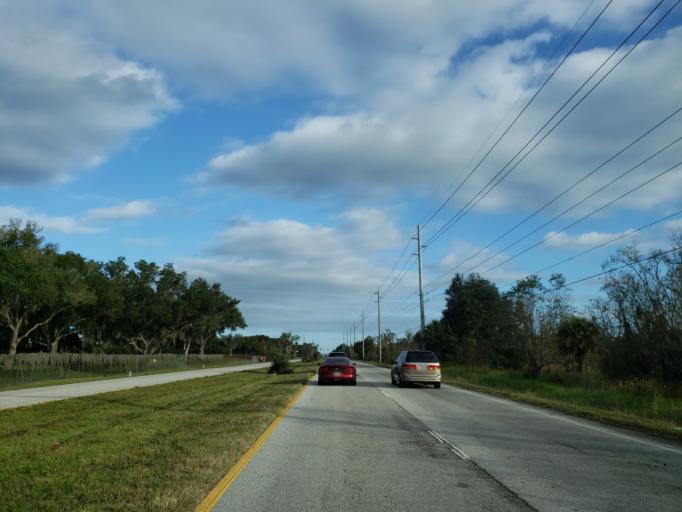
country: US
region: Florida
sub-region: Hillsborough County
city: Plant City
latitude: 28.0031
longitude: -82.1050
